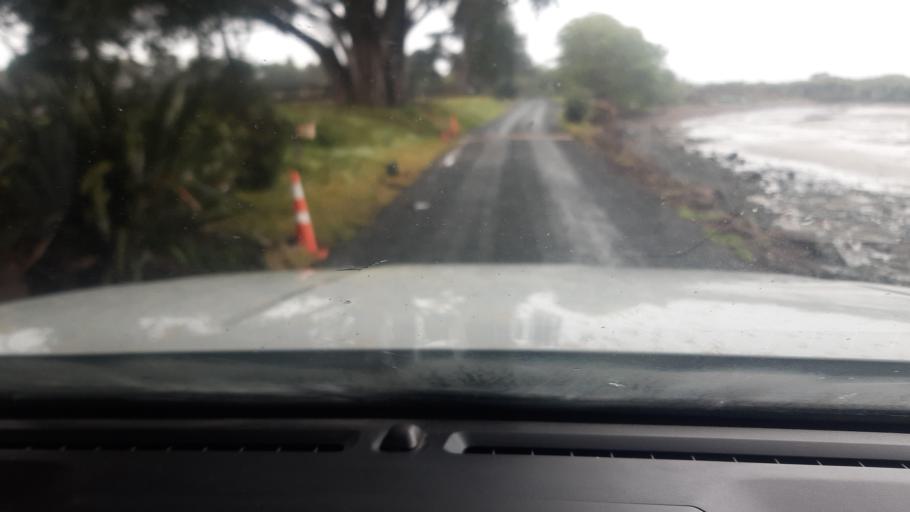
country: NZ
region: Northland
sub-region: Far North District
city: Kaitaia
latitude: -34.9180
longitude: 173.2673
